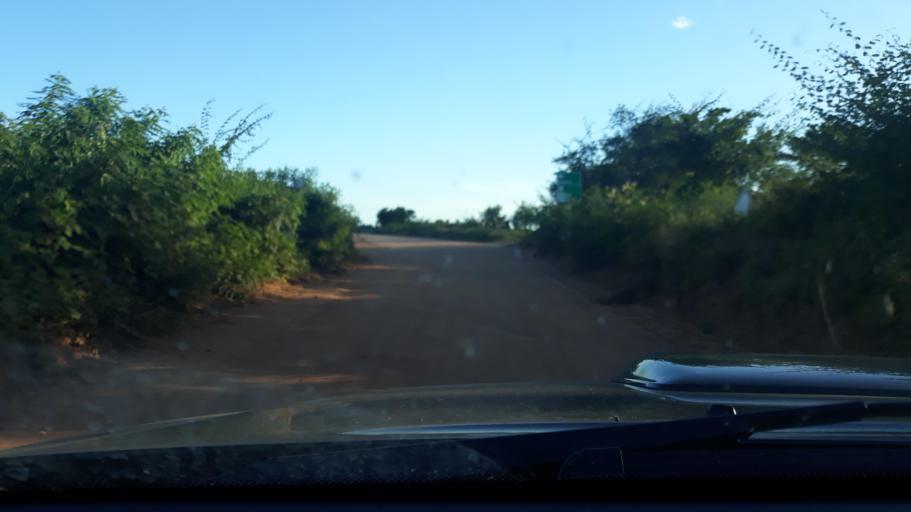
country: BR
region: Bahia
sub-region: Riacho De Santana
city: Riacho de Santana
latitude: -13.8001
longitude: -42.7129
